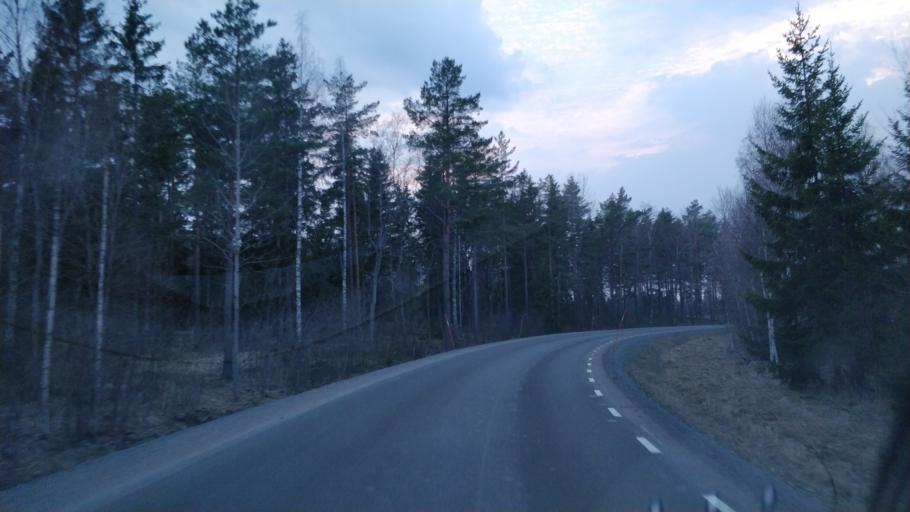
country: SE
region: Uppsala
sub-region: Enkopings Kommun
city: Orsundsbro
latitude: 59.7247
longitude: 17.2809
